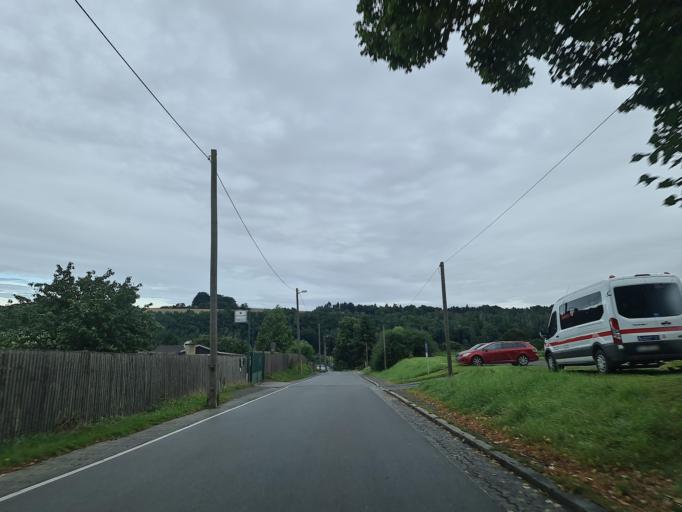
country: DE
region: Saxony
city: Plauen
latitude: 50.4850
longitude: 12.1128
